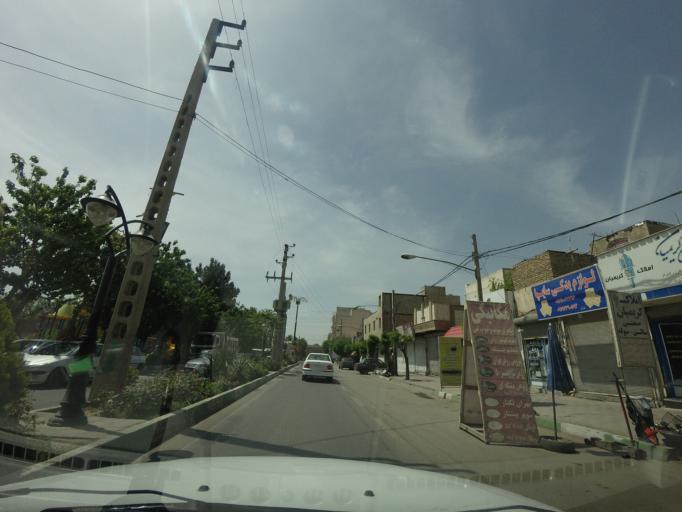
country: IR
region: Tehran
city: Eslamshahr
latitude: 35.6281
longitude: 51.2509
